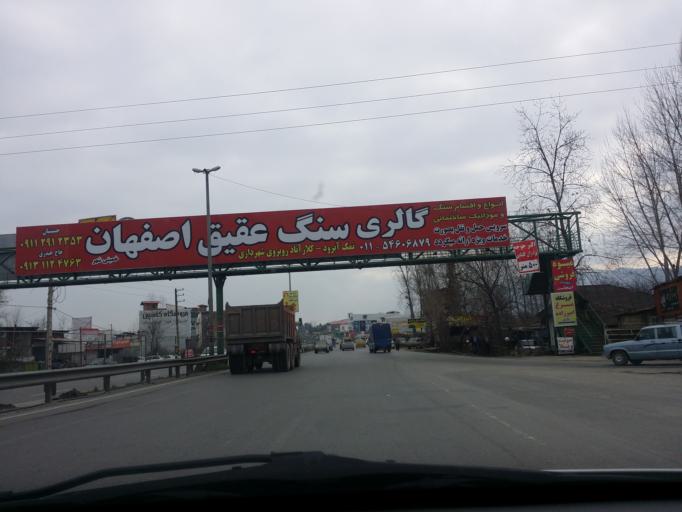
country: IR
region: Mazandaran
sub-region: Nowshahr
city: Nowshahr
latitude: 36.6381
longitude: 51.4890
